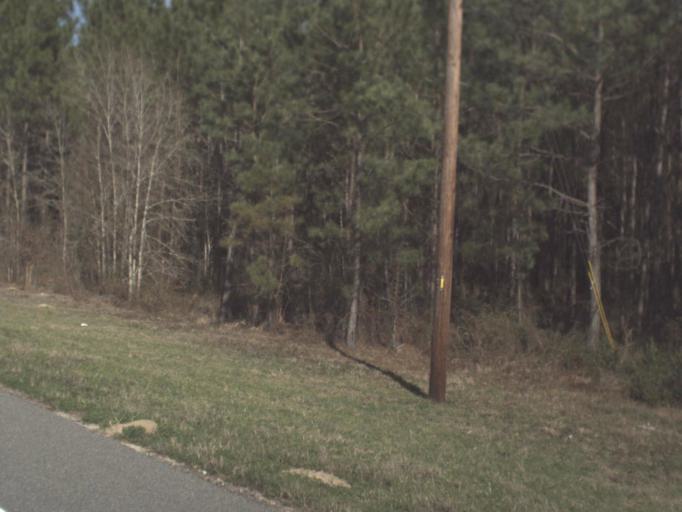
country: US
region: Florida
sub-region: Calhoun County
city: Blountstown
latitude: 30.3503
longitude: -85.2132
